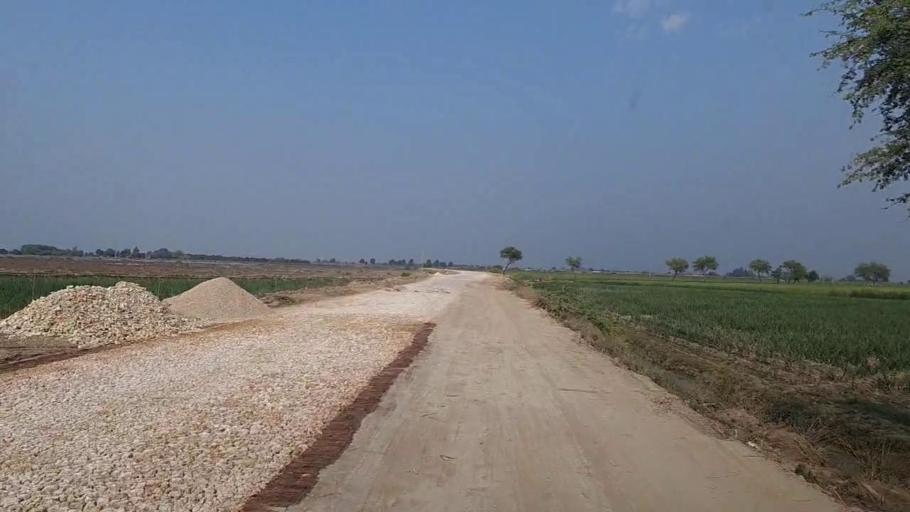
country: PK
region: Sindh
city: Mirwah Gorchani
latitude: 25.3964
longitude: 69.1374
